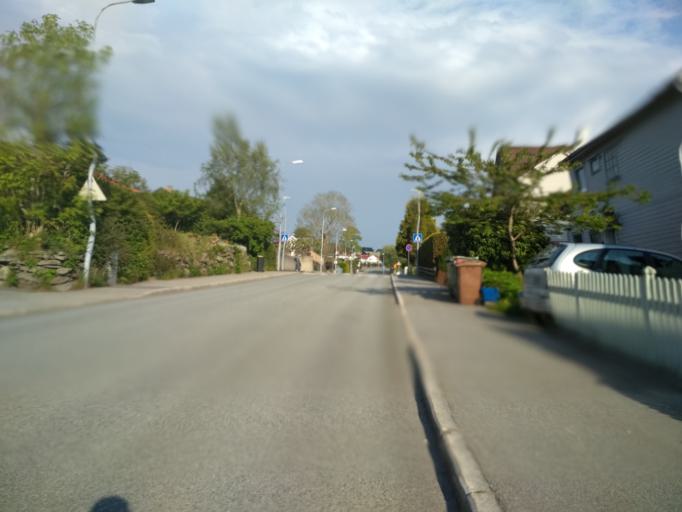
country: NO
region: Rogaland
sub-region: Stavanger
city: Stavanger
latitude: 58.9693
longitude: 5.7075
